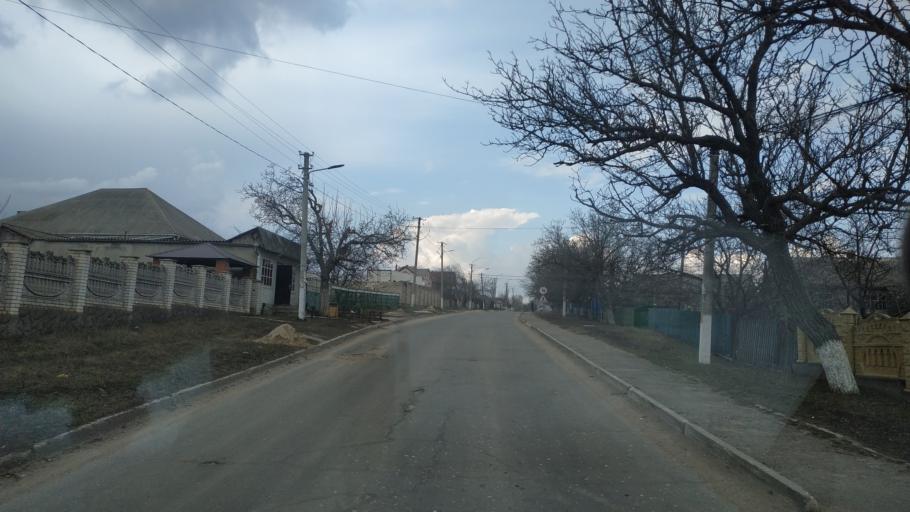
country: MD
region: Anenii Noi
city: Varnita
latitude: 46.8494
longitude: 29.3541
